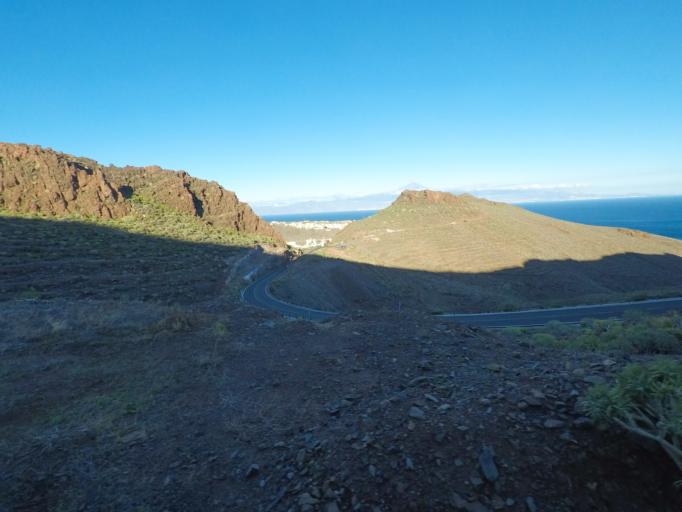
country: ES
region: Canary Islands
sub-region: Provincia de Santa Cruz de Tenerife
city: San Sebastian de la Gomera
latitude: 28.0824
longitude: -17.1280
